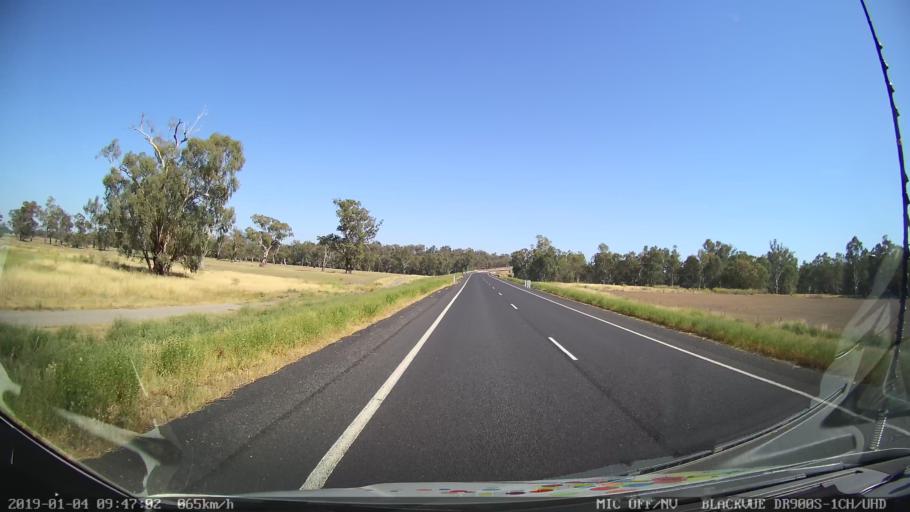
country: AU
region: New South Wales
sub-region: Cabonne
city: Canowindra
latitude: -33.6102
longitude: 148.4339
